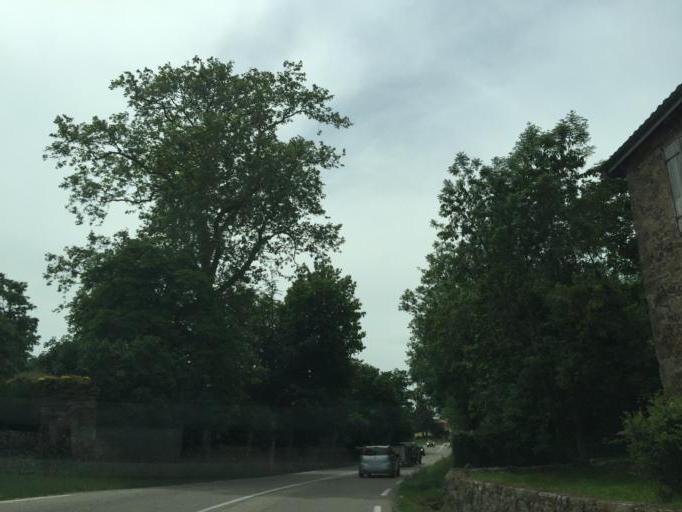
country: FR
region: Rhone-Alpes
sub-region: Departement de l'Ardeche
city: Boulieu-les-Annonay
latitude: 45.2629
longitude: 4.6673
